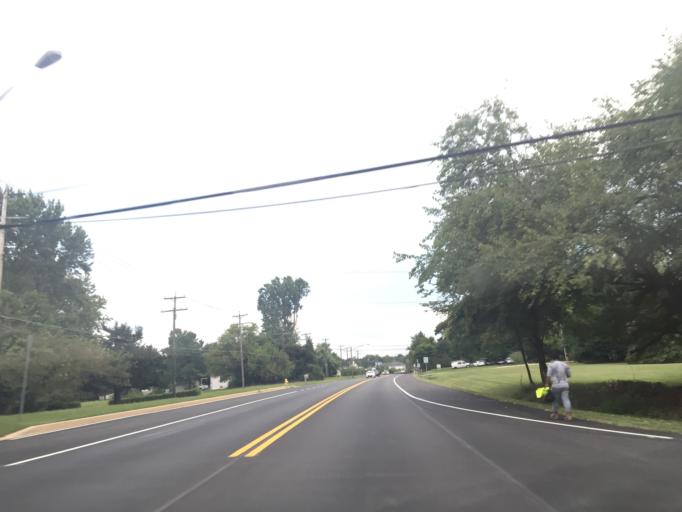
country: US
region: Maryland
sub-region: Anne Arundel County
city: Severn
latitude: 39.1409
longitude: -76.6850
